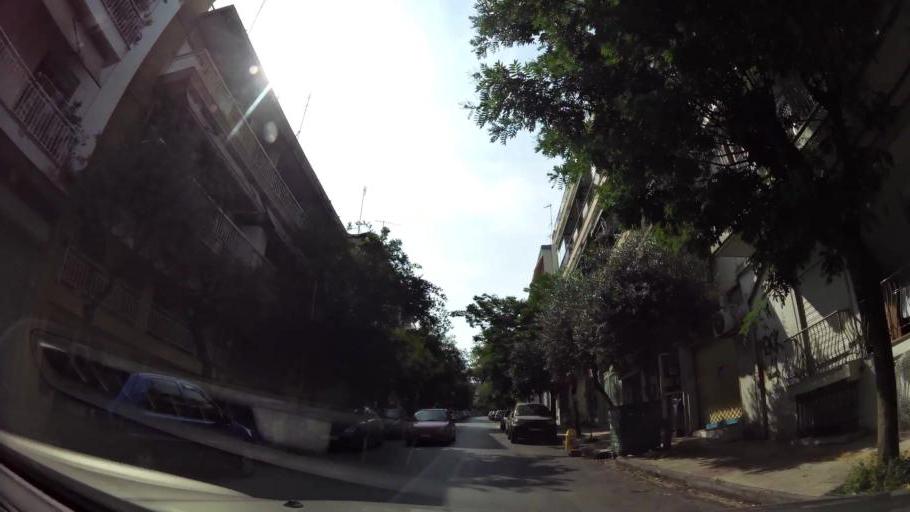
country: GR
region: Central Macedonia
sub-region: Nomos Thessalonikis
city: Sykies
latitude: 40.6489
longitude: 22.9472
